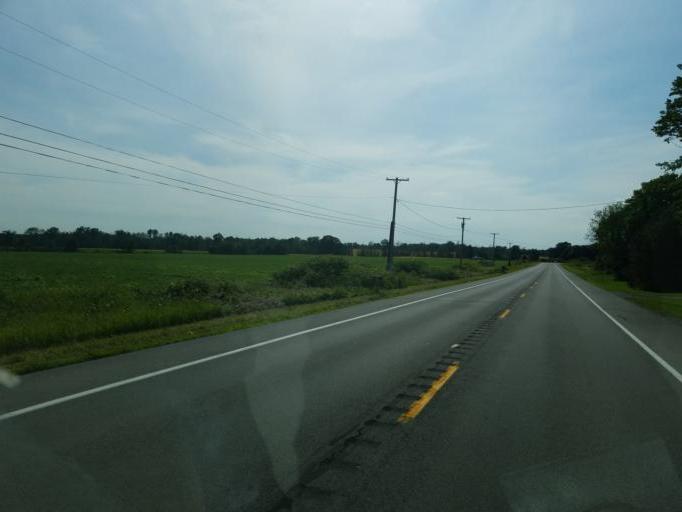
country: US
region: New York
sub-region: Livingston County
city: Caledonia
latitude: 42.9369
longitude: -77.8063
